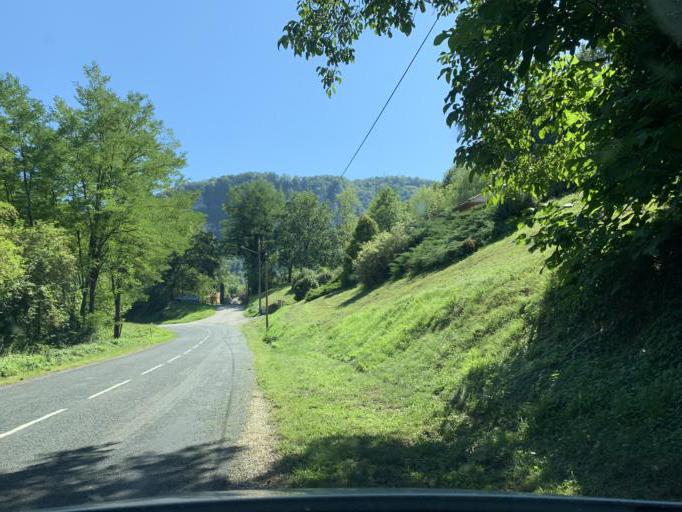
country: FR
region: Rhone-Alpes
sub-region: Departement de l'Ain
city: Saint-Rambert-en-Bugey
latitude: 45.9210
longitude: 5.4004
